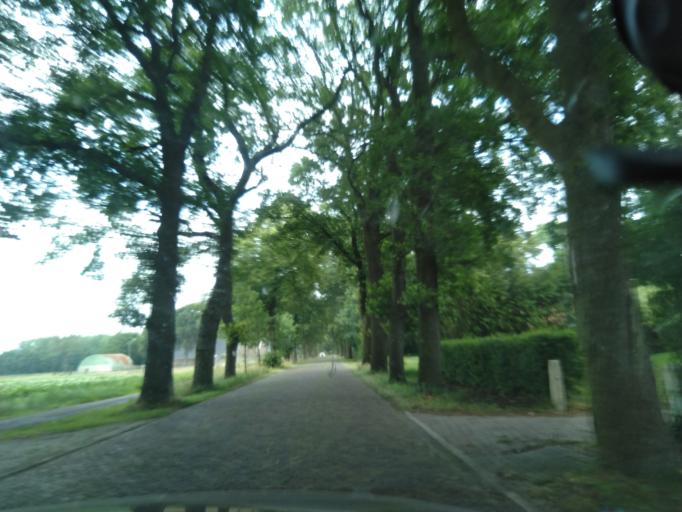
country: NL
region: Groningen
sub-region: Gemeente Vlagtwedde
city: Vlagtwedde
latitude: 53.0905
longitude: 7.1388
